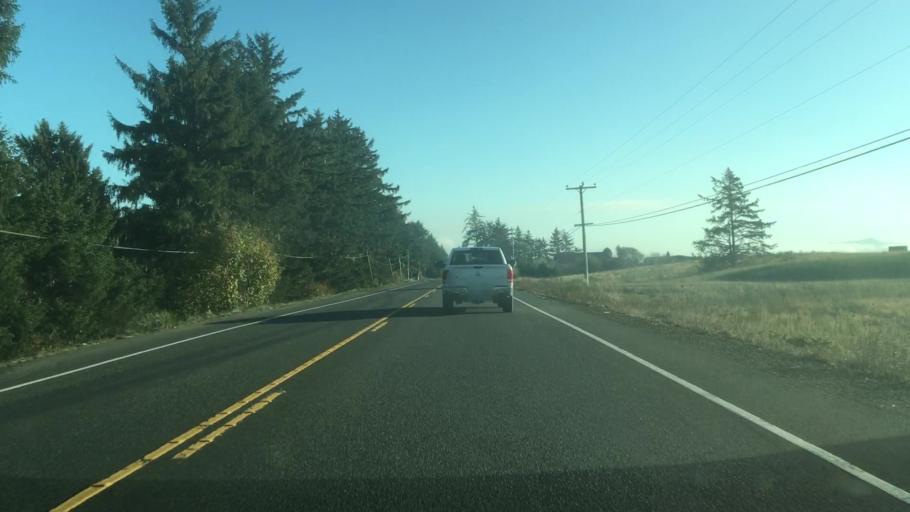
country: US
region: Oregon
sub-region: Clatsop County
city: Gearhart
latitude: 46.0909
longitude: -123.9169
